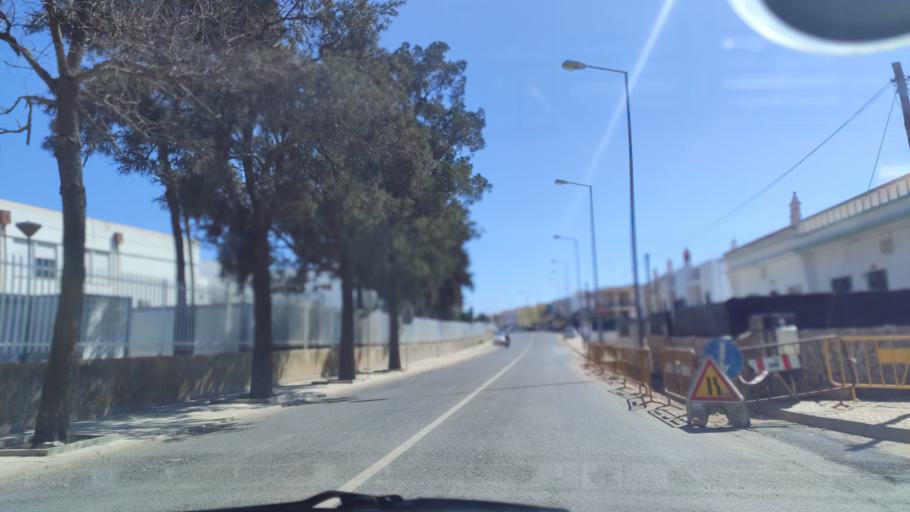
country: PT
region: Faro
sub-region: Olhao
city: Olhao
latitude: 37.0386
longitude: -7.8506
